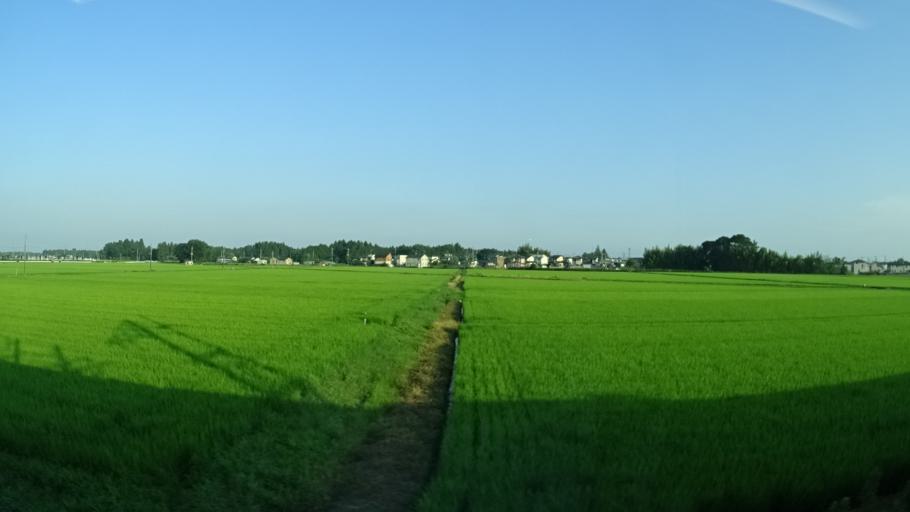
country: JP
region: Ibaraki
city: Tomobe
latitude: 36.3725
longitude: 140.3583
